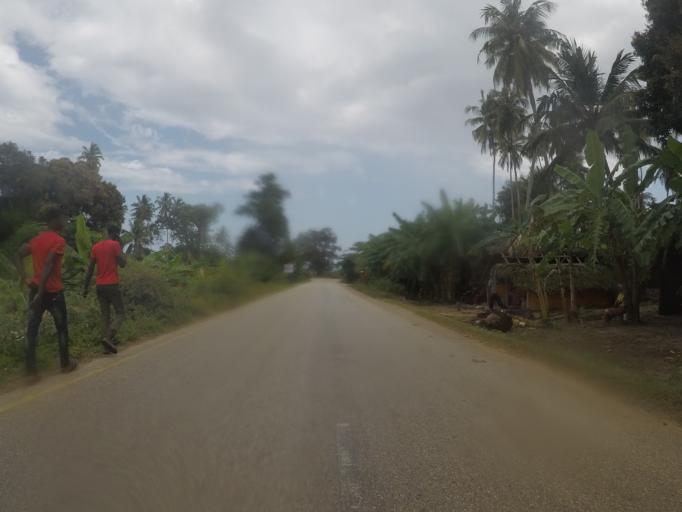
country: TZ
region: Zanzibar North
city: Mkokotoni
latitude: -5.9931
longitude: 39.1870
